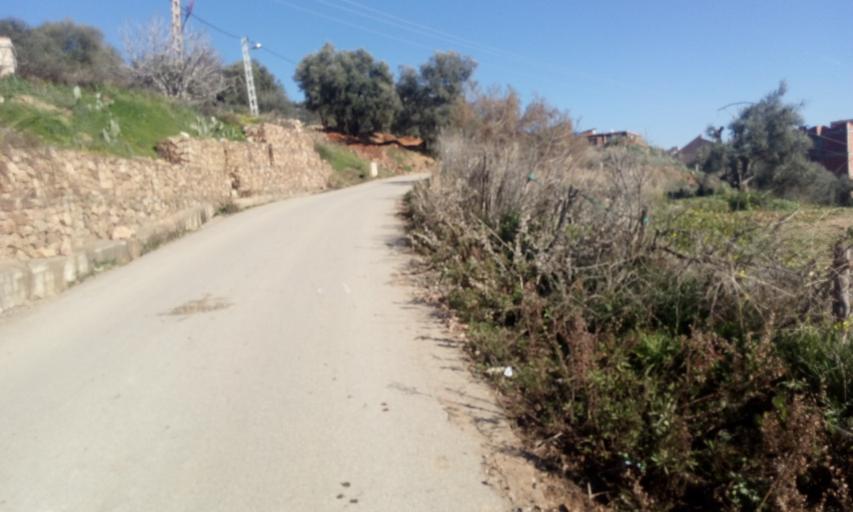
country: DZ
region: Tizi Ouzou
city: Chemini
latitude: 36.6028
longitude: 4.6390
